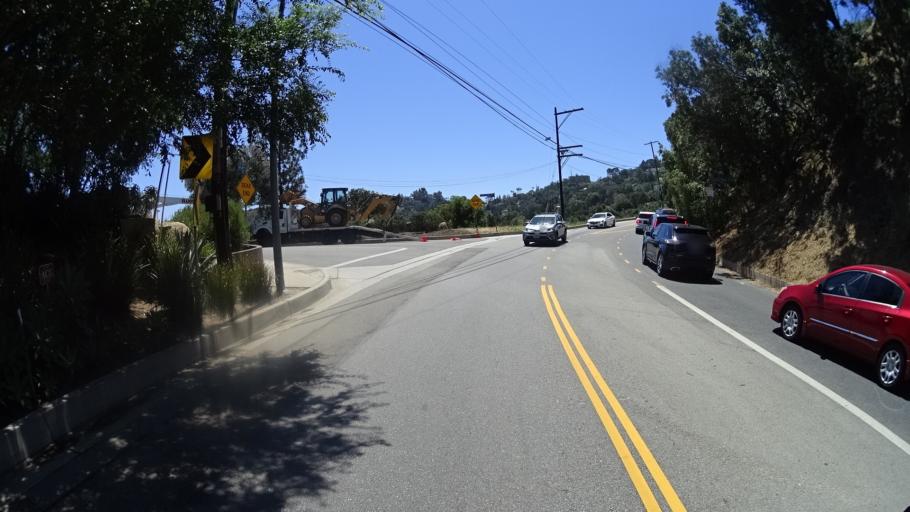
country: US
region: California
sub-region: Los Angeles County
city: Sherman Oaks
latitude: 34.1343
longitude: -118.4487
